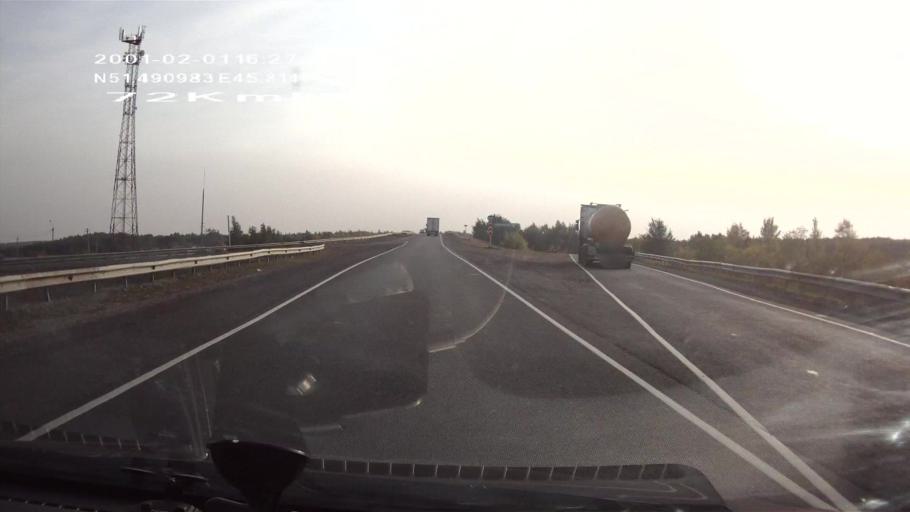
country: RU
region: Saratov
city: Sokolovyy
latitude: 51.4907
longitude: 45.8139
